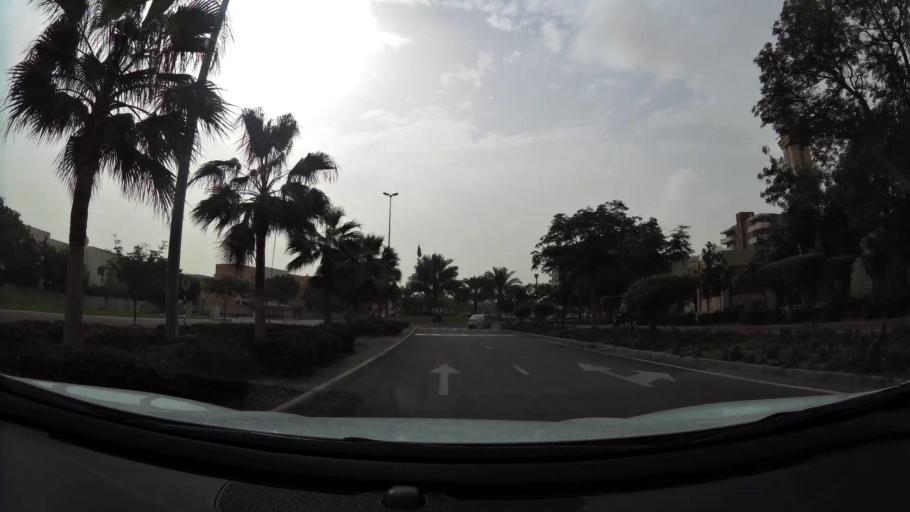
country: AE
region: Abu Dhabi
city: Abu Dhabi
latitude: 24.4589
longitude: 54.6737
